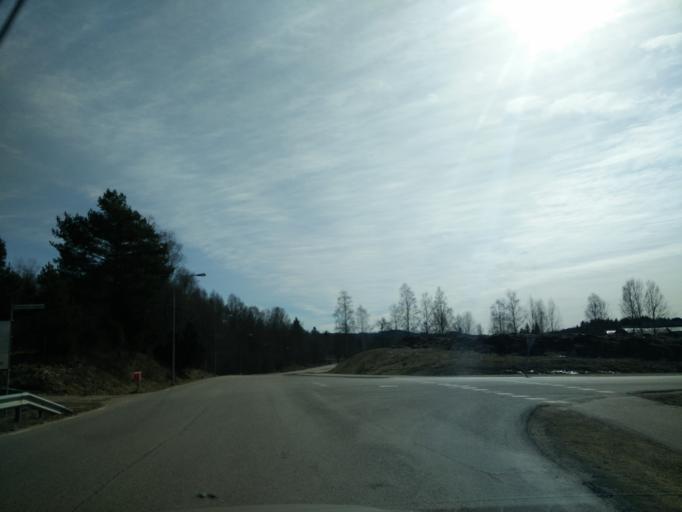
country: SE
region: Vaermland
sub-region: Hagfors Kommun
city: Hagfors
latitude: 60.0252
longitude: 13.6928
